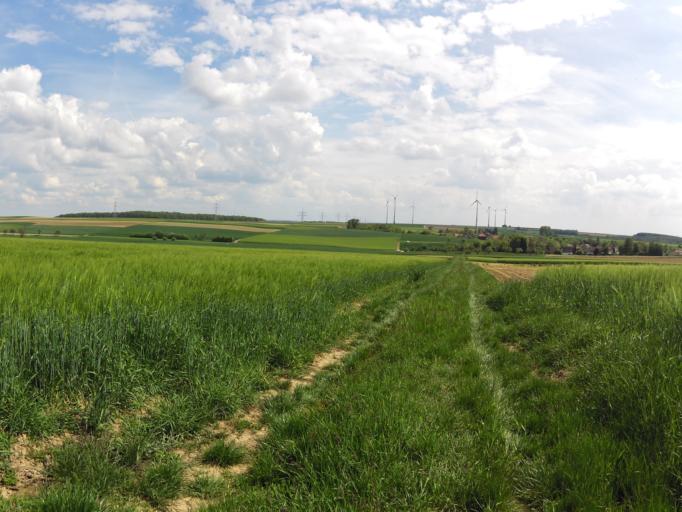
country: DE
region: Bavaria
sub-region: Regierungsbezirk Unterfranken
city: Theilheim
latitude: 49.7405
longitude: 10.0318
